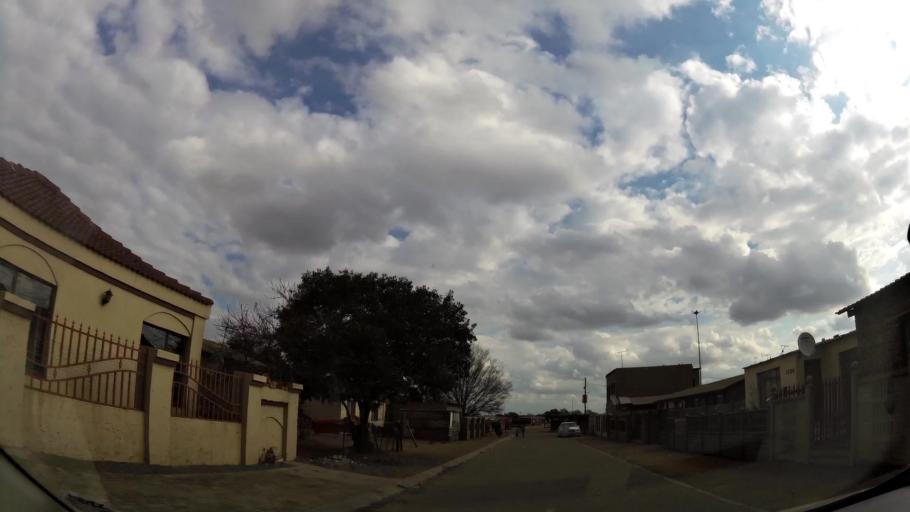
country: ZA
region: Orange Free State
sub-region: Fezile Dabi District Municipality
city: Sasolburg
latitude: -26.8395
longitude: 27.8460
